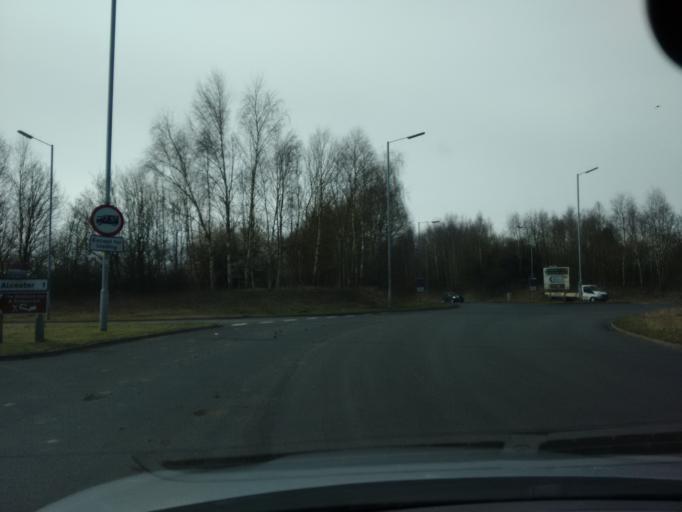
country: GB
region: England
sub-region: Warwickshire
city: Alcester
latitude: 52.2242
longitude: -1.8795
